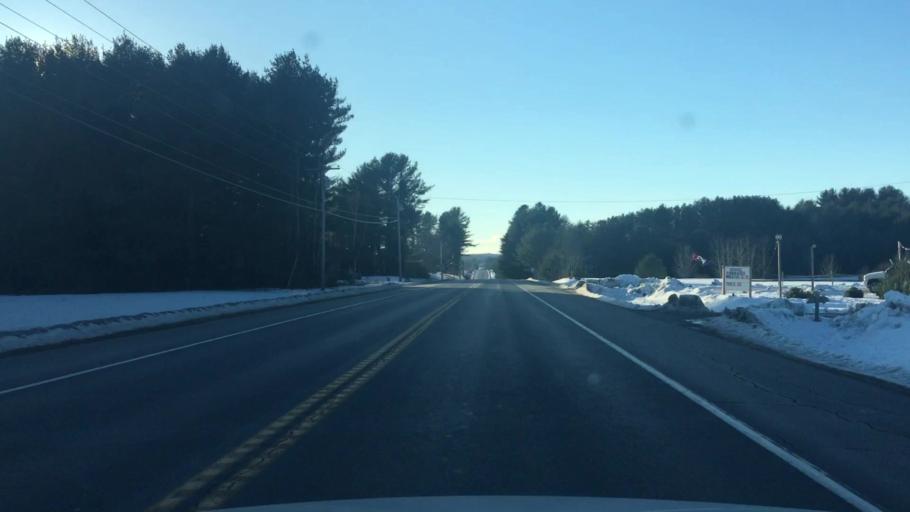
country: US
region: Maine
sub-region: Somerset County
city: Norridgewock
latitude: 44.7063
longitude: -69.8151
